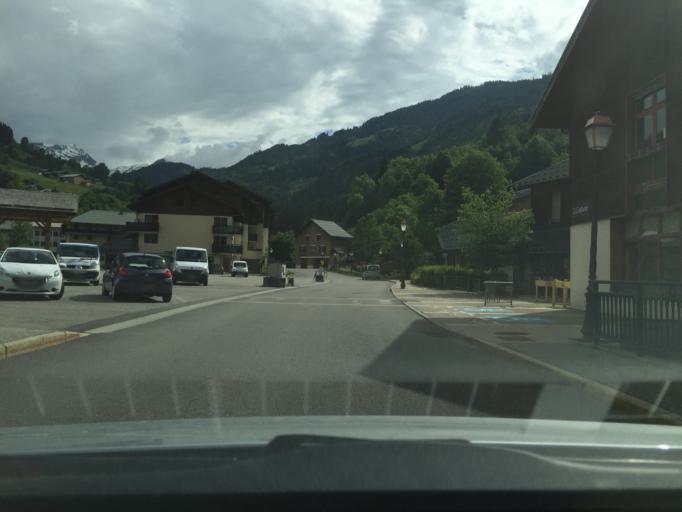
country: FR
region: Rhone-Alpes
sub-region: Departement de la Savoie
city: Beaufort
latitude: 45.7188
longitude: 6.5737
